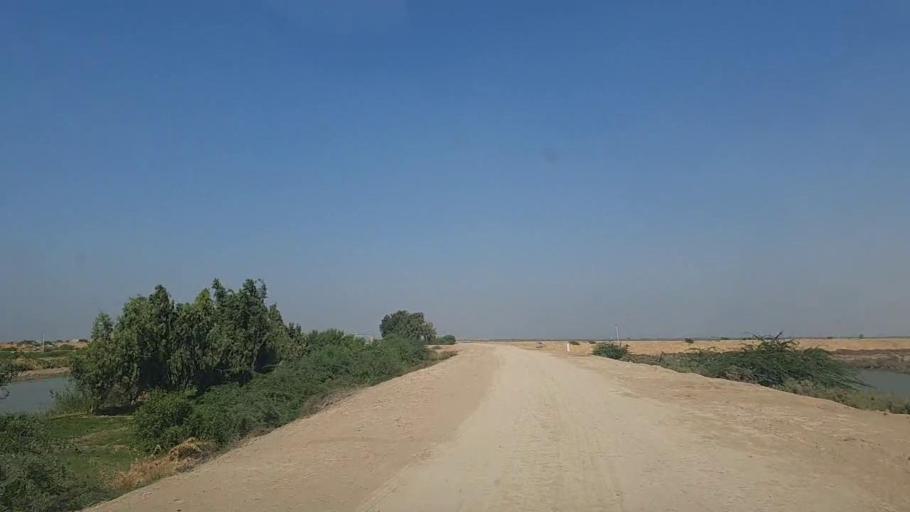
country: PK
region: Sindh
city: Daro Mehar
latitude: 24.9123
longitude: 68.0781
